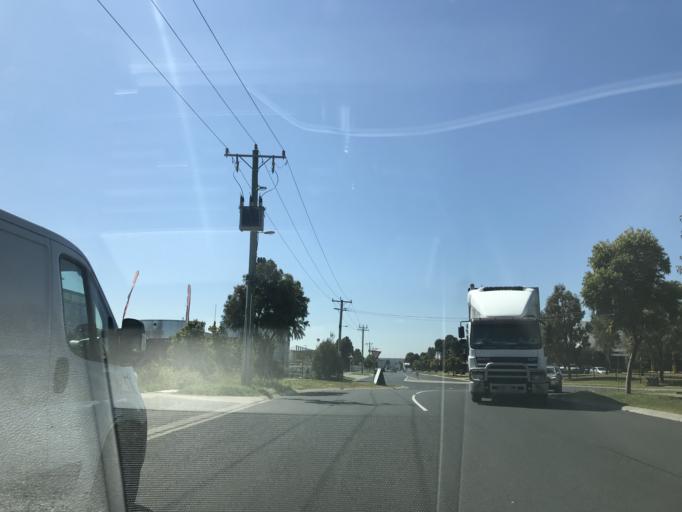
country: AU
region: Victoria
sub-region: Wyndham
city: Truganina
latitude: -37.8229
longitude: 144.7717
